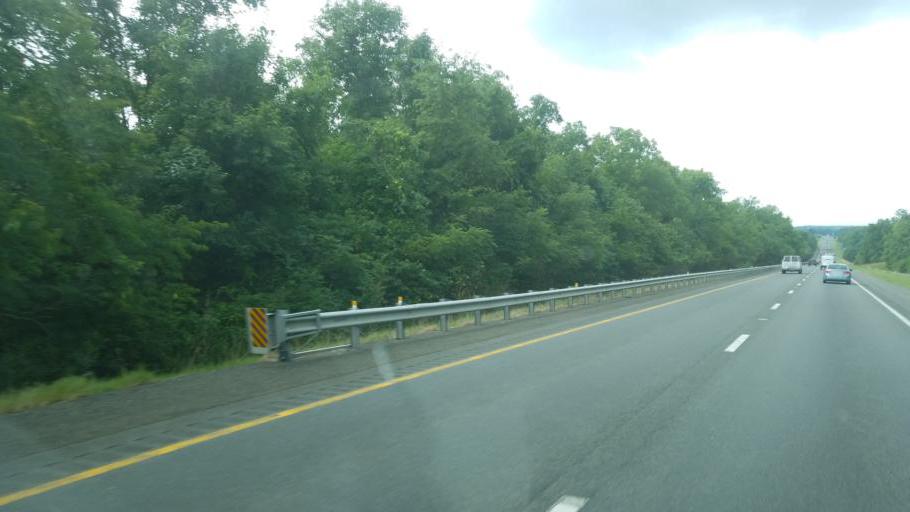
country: US
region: Virginia
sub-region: Warren County
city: Front Royal
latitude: 38.9479
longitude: -78.1555
